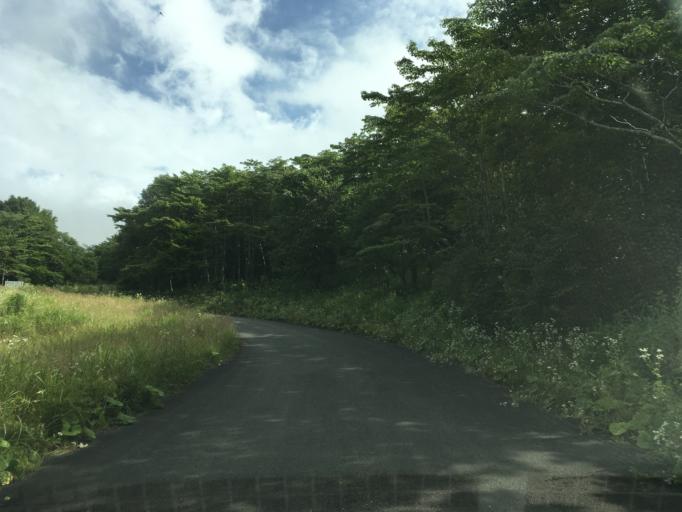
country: JP
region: Iwate
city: Ofunato
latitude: 38.9817
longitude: 141.4522
